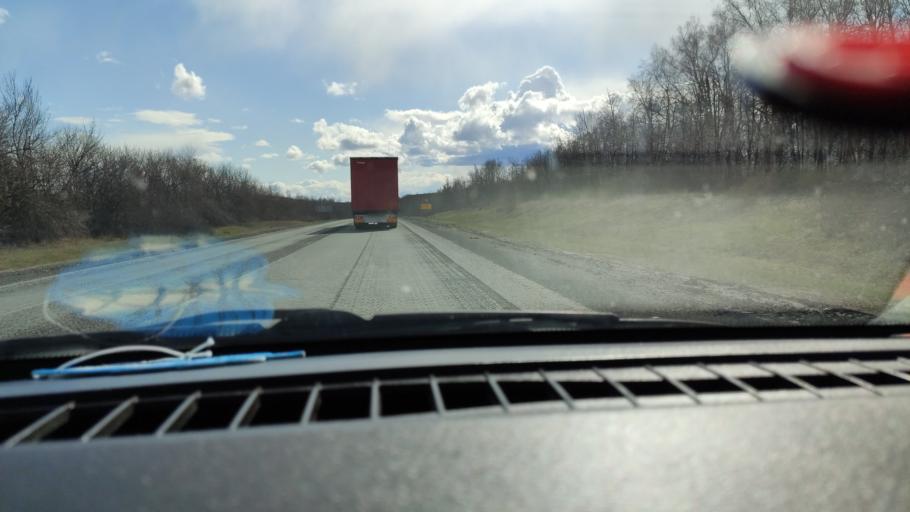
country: RU
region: Saratov
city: Dukhovnitskoye
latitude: 52.6314
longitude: 48.1843
